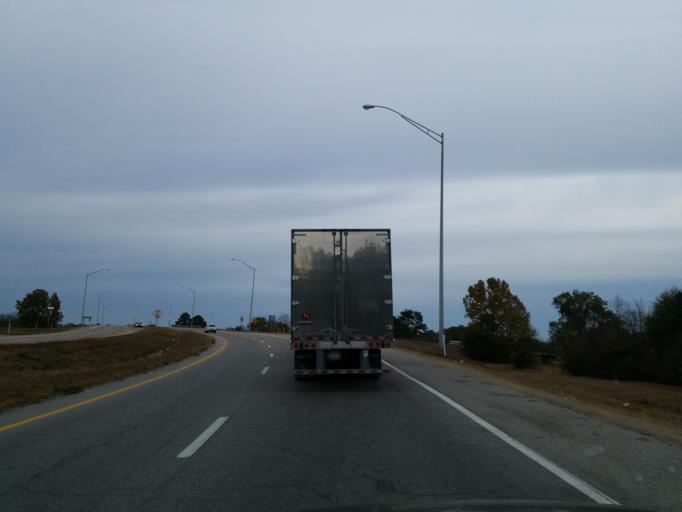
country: US
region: Mississippi
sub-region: Lauderdale County
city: Meridian
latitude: 32.3465
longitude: -88.7266
